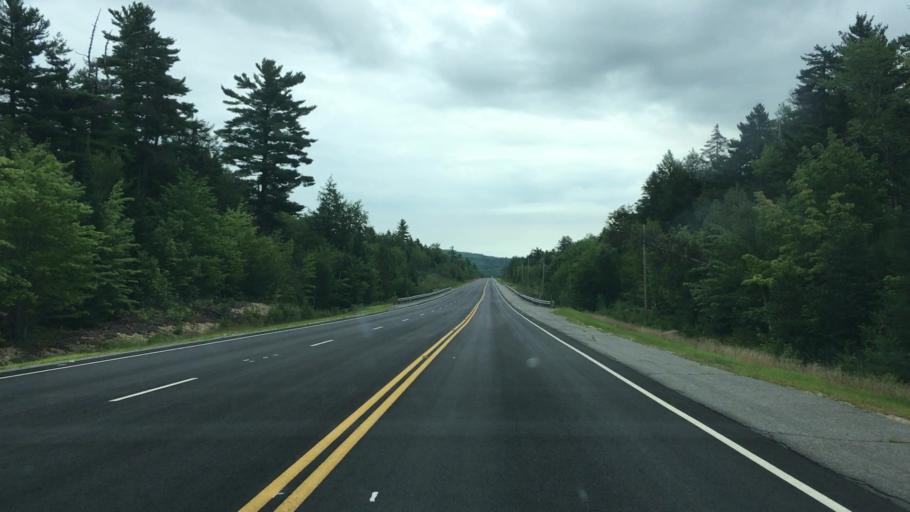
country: US
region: Maine
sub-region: Washington County
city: Cherryfield
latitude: 44.8749
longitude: -67.8977
